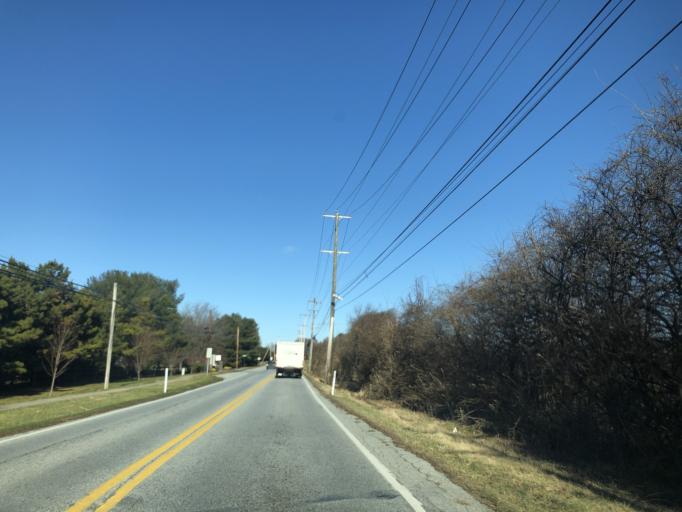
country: US
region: Pennsylvania
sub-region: Chester County
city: Kennett Square
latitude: 39.8880
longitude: -75.7219
